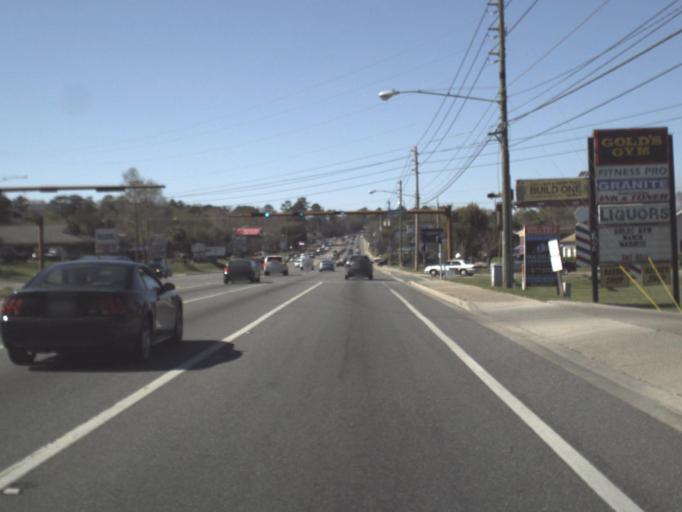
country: US
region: Florida
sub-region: Leon County
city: Tallahassee
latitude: 30.4878
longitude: -84.2387
